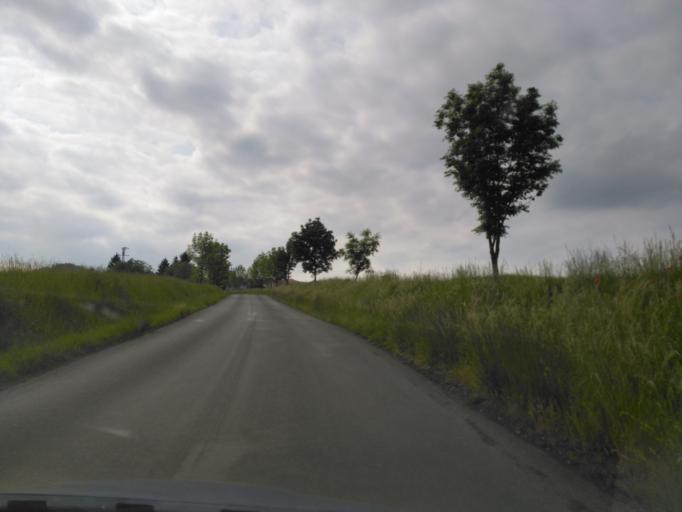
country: CZ
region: Central Bohemia
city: Hudlice
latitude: 49.9582
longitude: 13.9826
